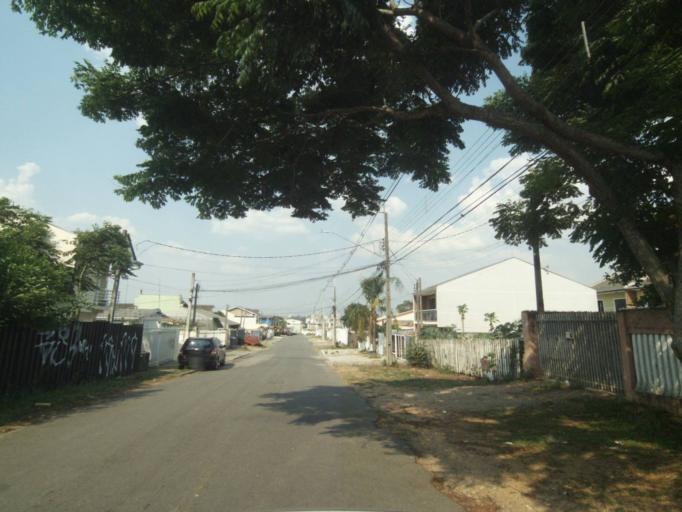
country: BR
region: Parana
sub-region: Sao Jose Dos Pinhais
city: Sao Jose dos Pinhais
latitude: -25.5352
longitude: -49.2383
